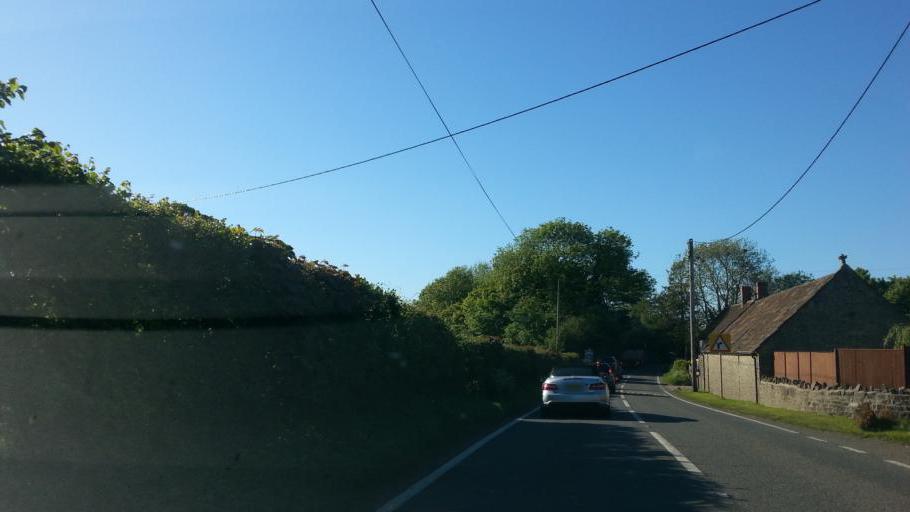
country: GB
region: England
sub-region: Somerset
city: Castle Cary
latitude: 51.1193
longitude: -2.5175
